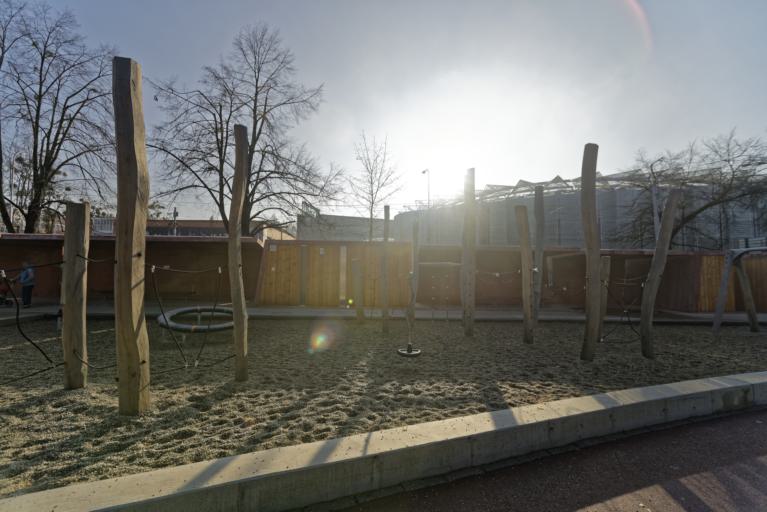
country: CZ
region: Zlin
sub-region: Okres Zlin
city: Zlin
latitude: 49.2238
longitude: 17.6649
